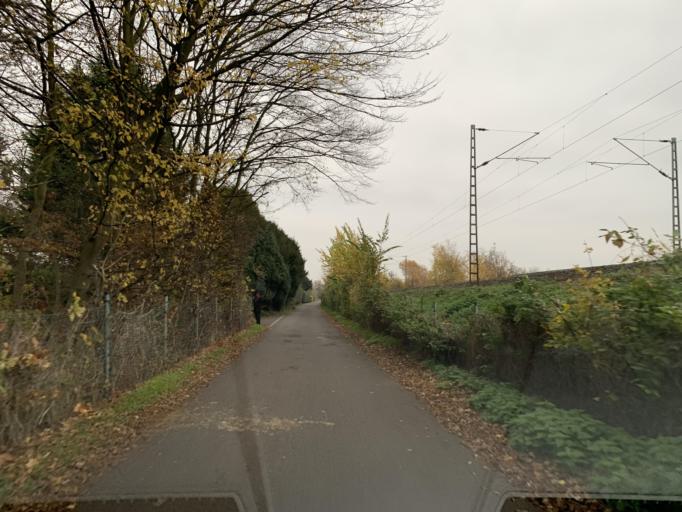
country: DE
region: North Rhine-Westphalia
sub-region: Regierungsbezirk Munster
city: Muenster
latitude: 51.9747
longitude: 7.6531
